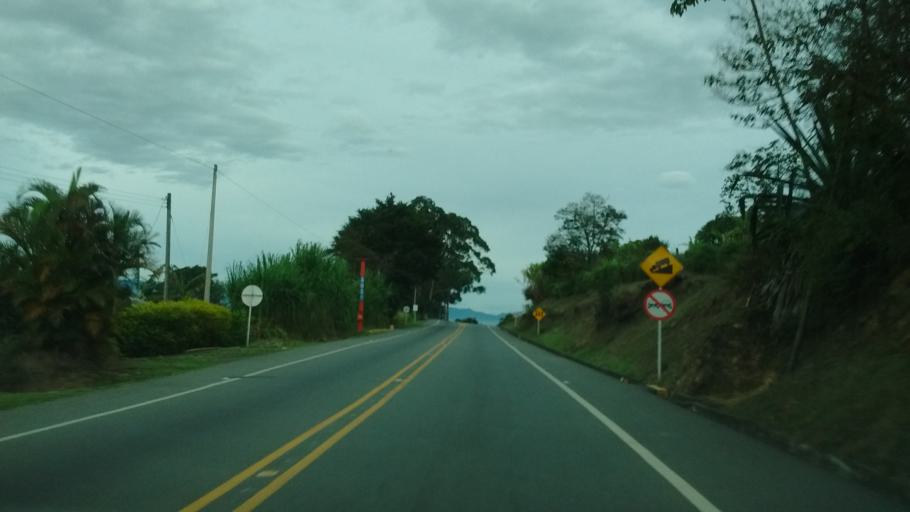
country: CO
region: Cauca
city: Morales
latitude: 2.7143
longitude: -76.5406
